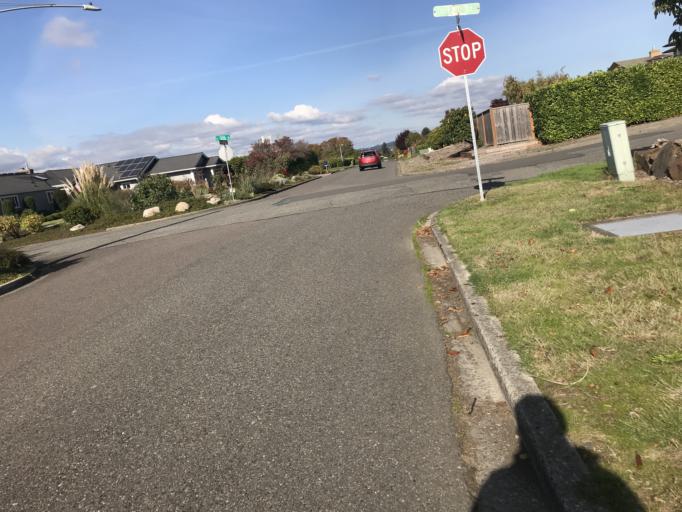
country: US
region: Washington
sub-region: Pierce County
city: University Place
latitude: 47.2498
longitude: -122.5423
